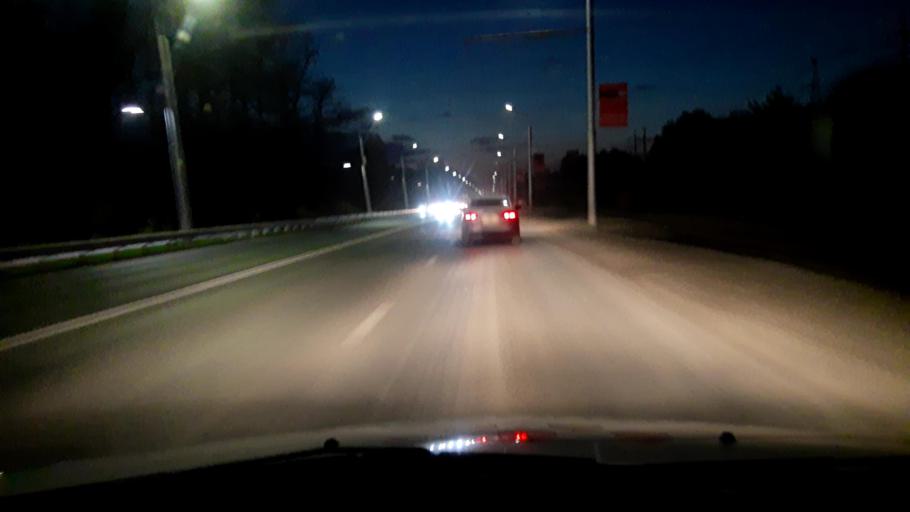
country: RU
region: Bashkortostan
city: Ufa
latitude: 54.7889
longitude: 56.1113
